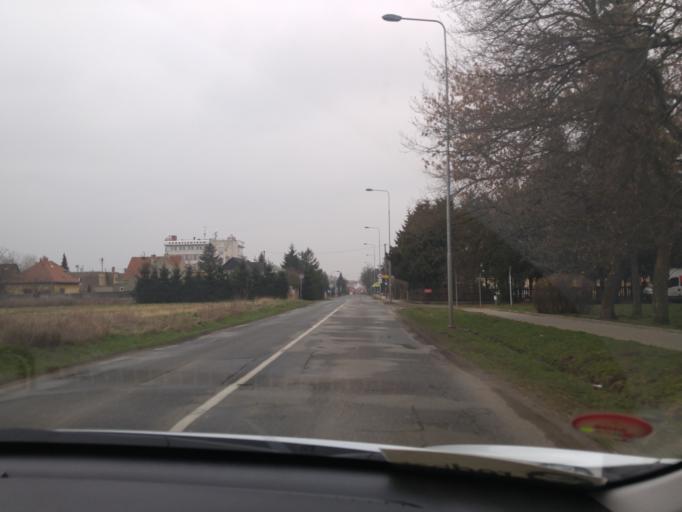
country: CZ
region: Central Bohemia
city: Brandys nad Labem-Stara Boleslav
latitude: 50.1908
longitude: 14.6478
